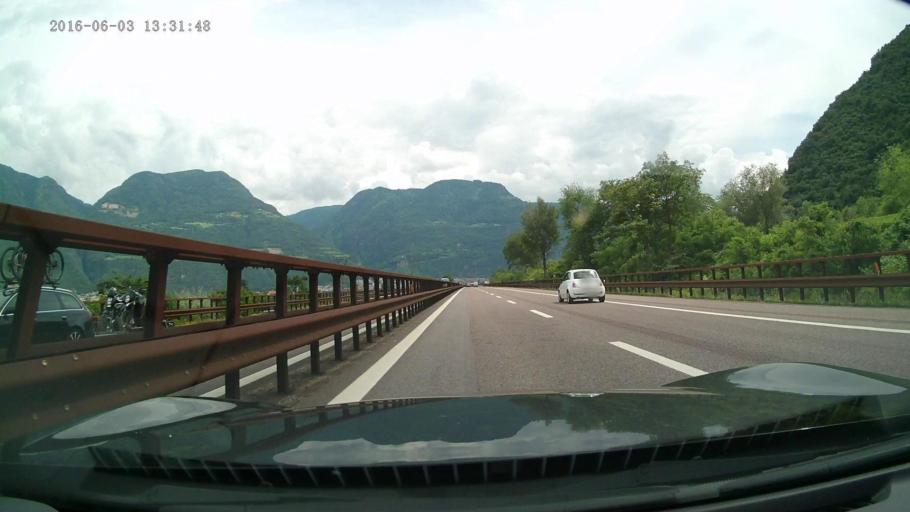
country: IT
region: Trentino-Alto Adige
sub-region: Bolzano
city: San Giacomo
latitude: 46.4460
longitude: 11.3124
